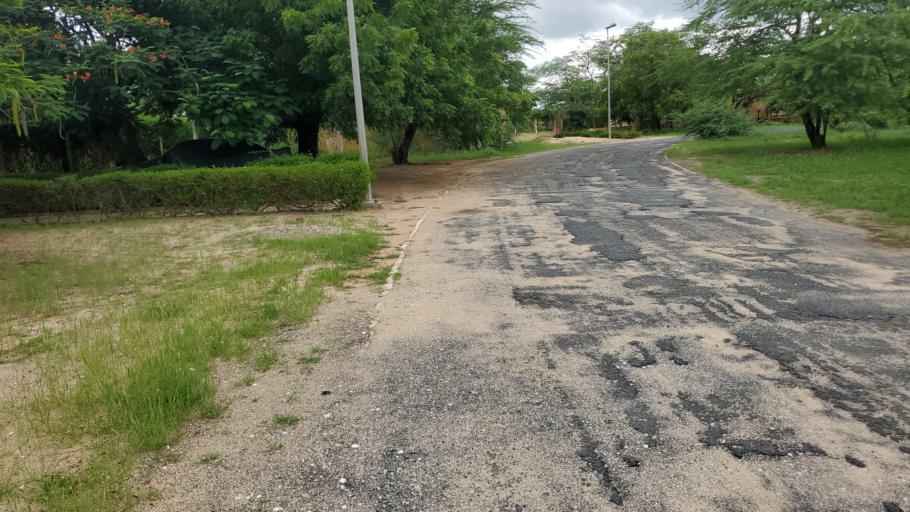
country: SN
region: Saint-Louis
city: Saint-Louis
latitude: 16.0693
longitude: -16.4200
